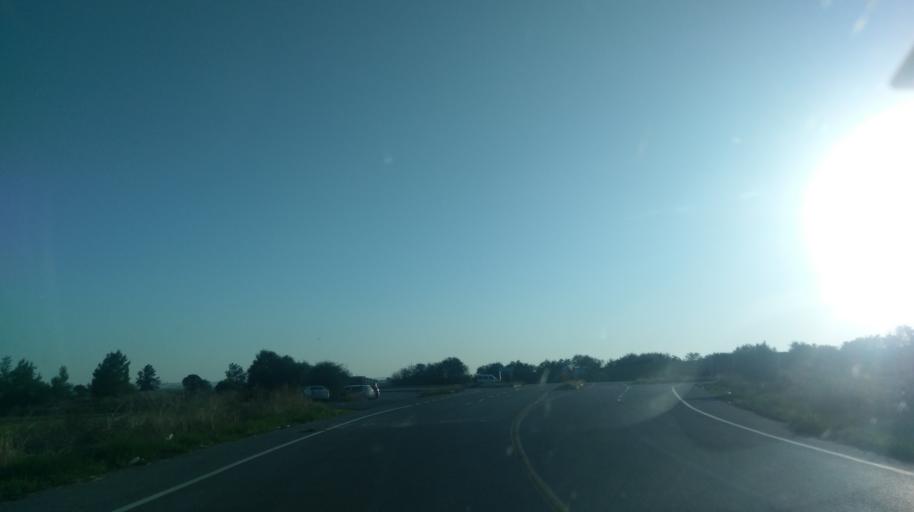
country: CY
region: Ammochostos
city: Lefkonoiko
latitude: 35.1961
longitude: 33.6189
